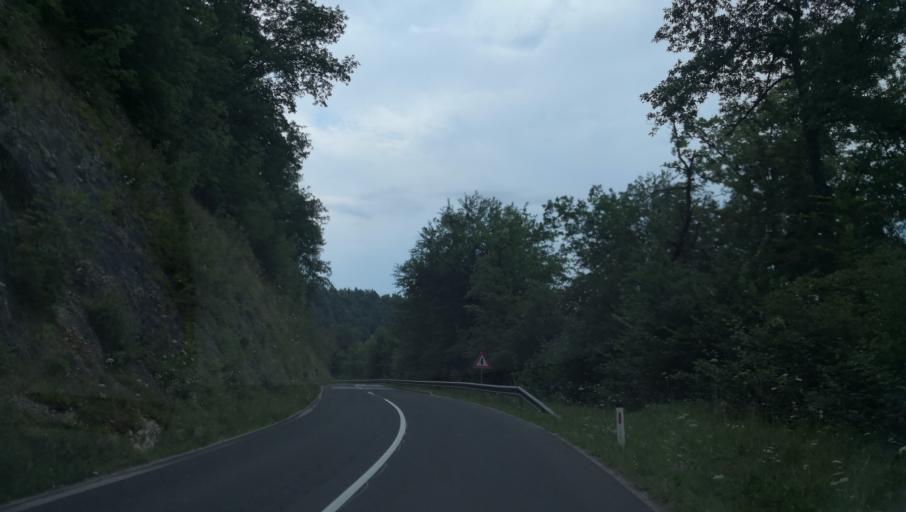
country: SI
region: Zuzemberk
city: Zuzemberk
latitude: 45.8523
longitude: 14.8978
